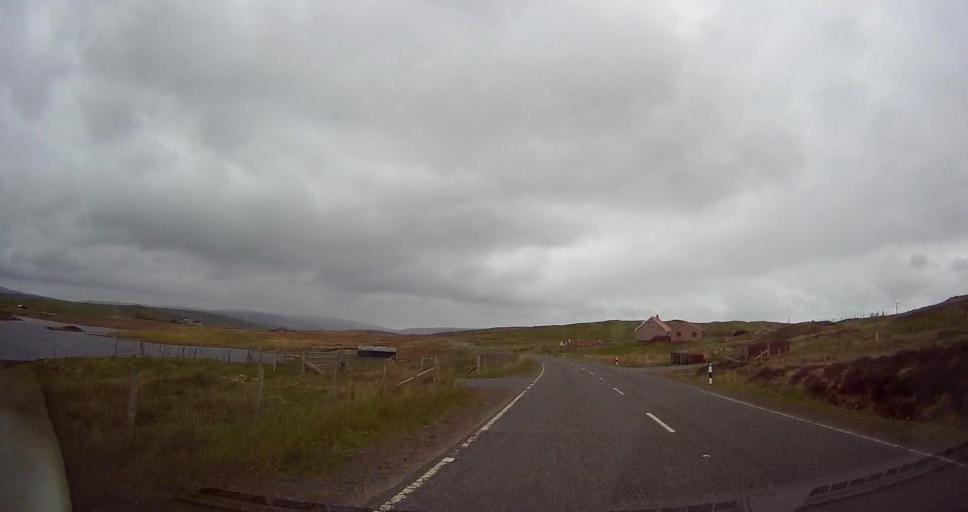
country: GB
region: Scotland
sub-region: Shetland Islands
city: Lerwick
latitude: 60.2563
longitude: -1.4671
